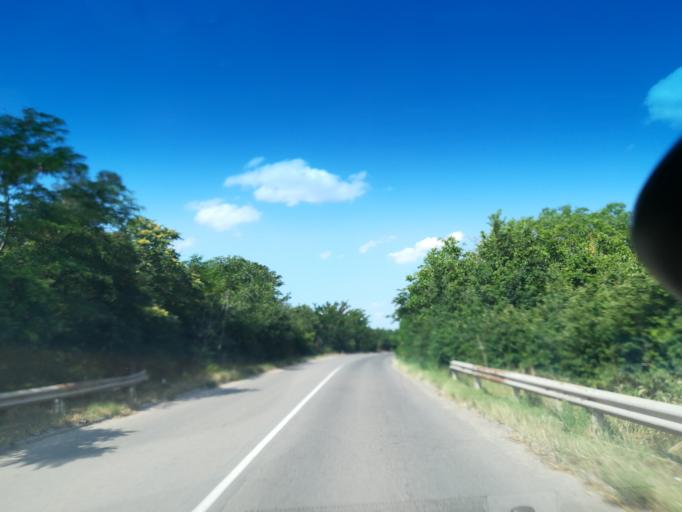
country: BG
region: Stara Zagora
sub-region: Obshtina Chirpan
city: Chirpan
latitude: 42.2173
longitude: 25.3748
